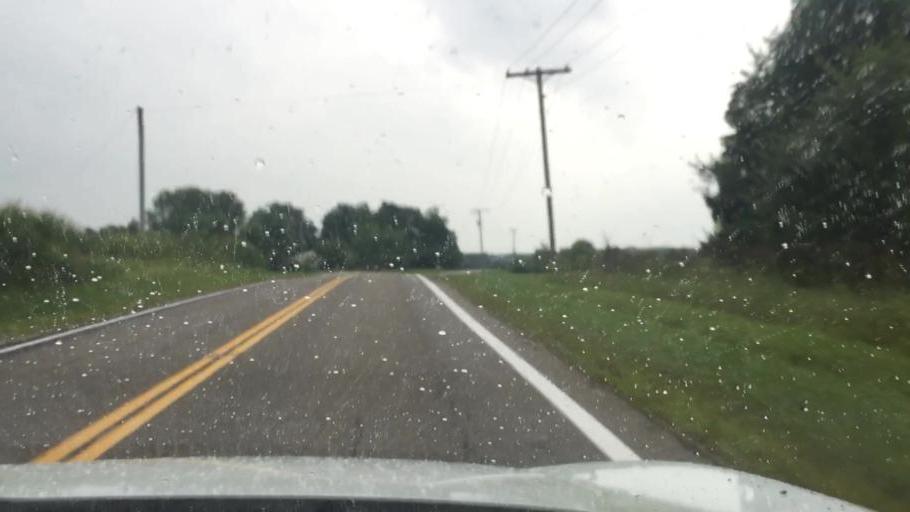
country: US
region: Ohio
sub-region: Champaign County
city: Mechanicsburg
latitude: 40.0984
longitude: -83.5745
